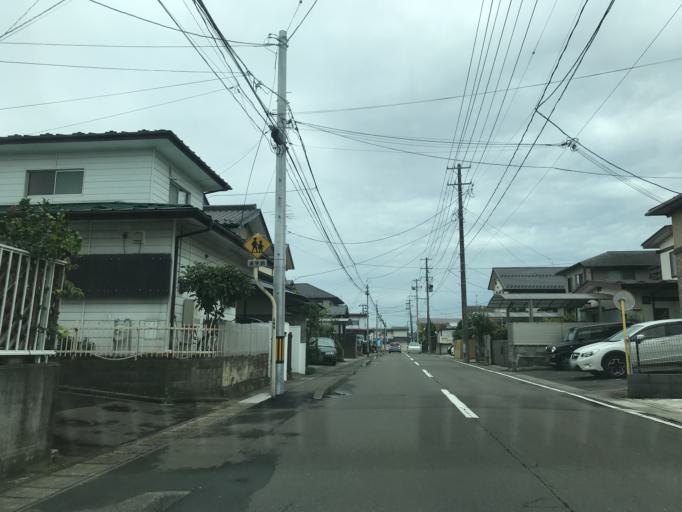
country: JP
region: Miyagi
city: Sendai-shi
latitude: 38.3060
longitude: 140.8943
